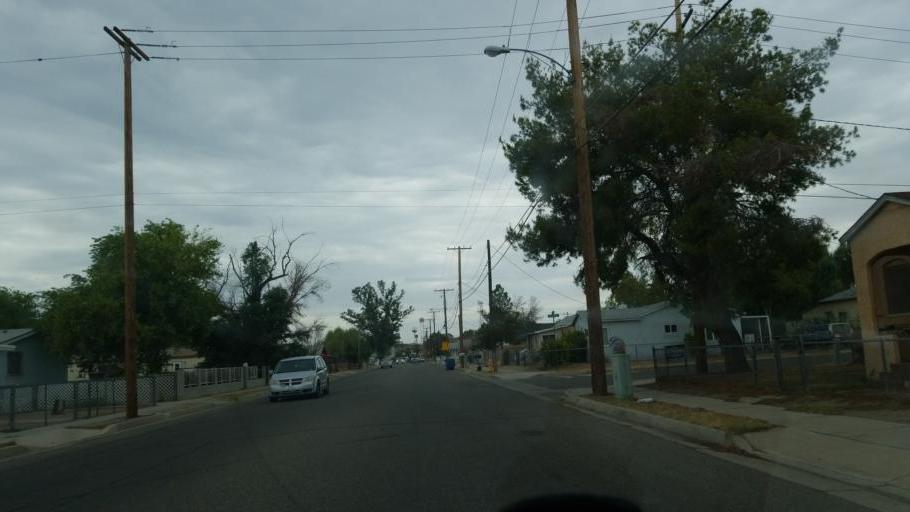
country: US
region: California
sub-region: San Bernardino County
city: Needles
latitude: 34.8470
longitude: -114.6105
